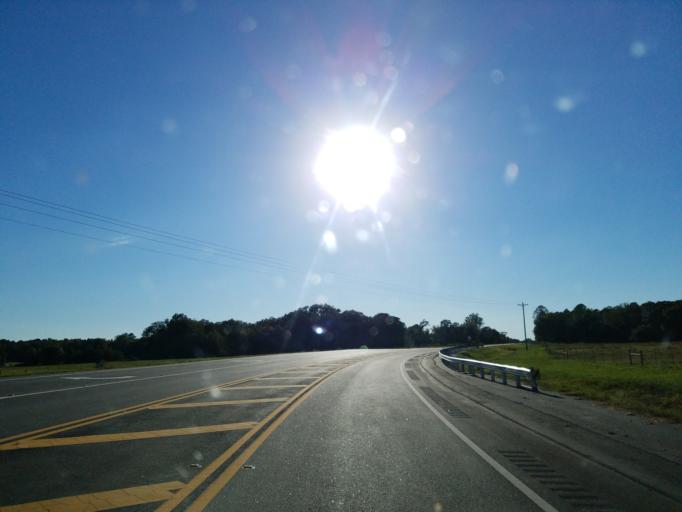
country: US
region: Georgia
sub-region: Lee County
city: Leesburg
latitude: 31.7502
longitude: -84.1582
